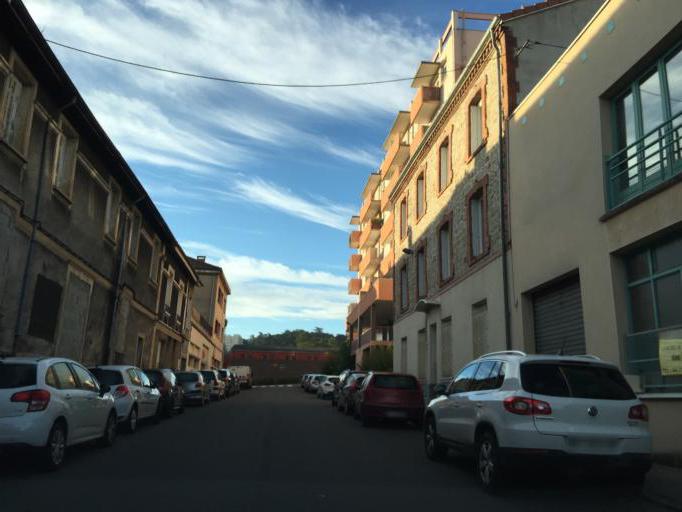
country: FR
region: Rhone-Alpes
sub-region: Departement de la Loire
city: Saint-Priest-en-Jarez
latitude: 45.4653
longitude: 4.3769
